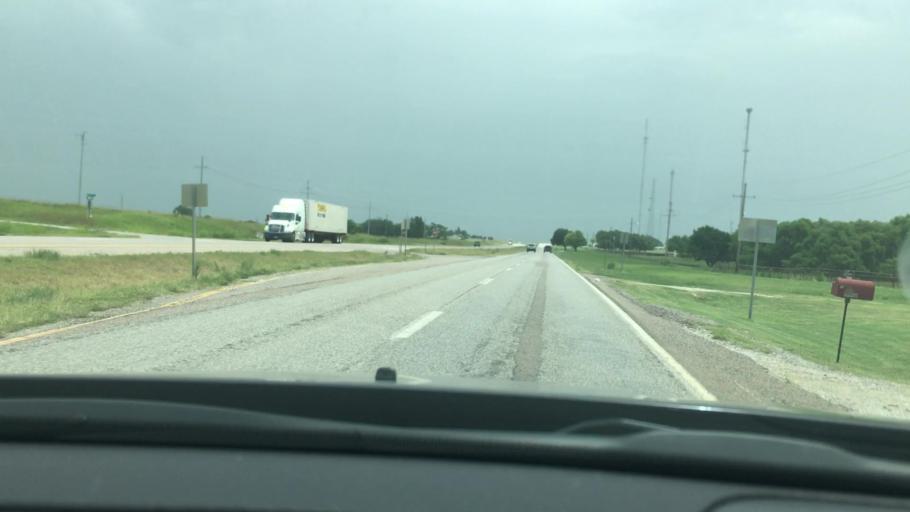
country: US
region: Oklahoma
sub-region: Pontotoc County
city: Ada
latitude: 34.6791
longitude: -96.7699
